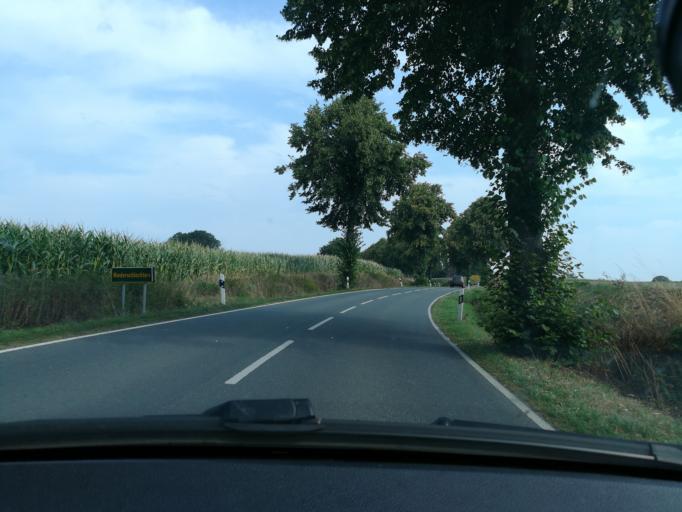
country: DE
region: Lower Saxony
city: Melle
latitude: 52.1601
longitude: 8.3312
